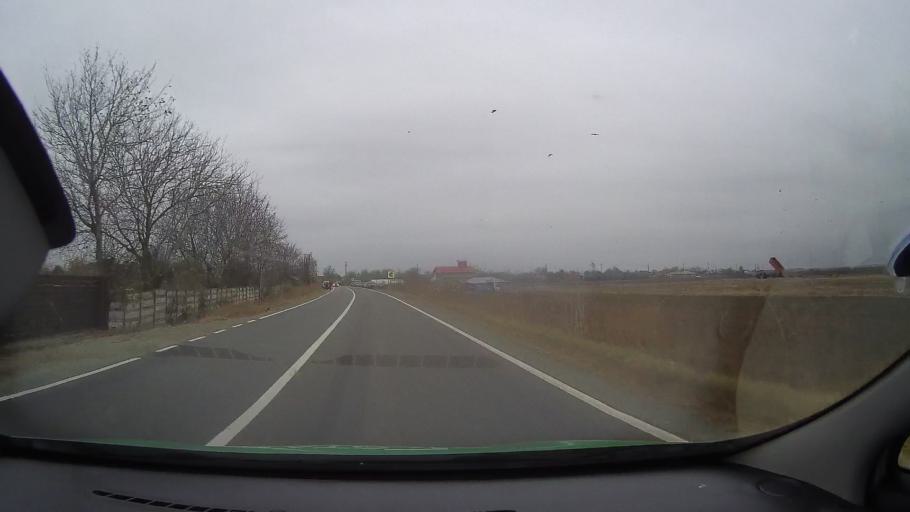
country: RO
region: Ialomita
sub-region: Comuna Slobozia
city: Slobozia
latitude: 44.6090
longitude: 27.3850
